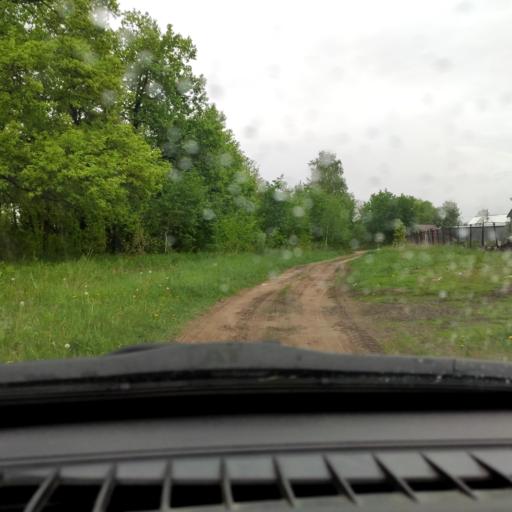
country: RU
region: Samara
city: Zhigulevsk
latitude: 53.5177
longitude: 49.5529
